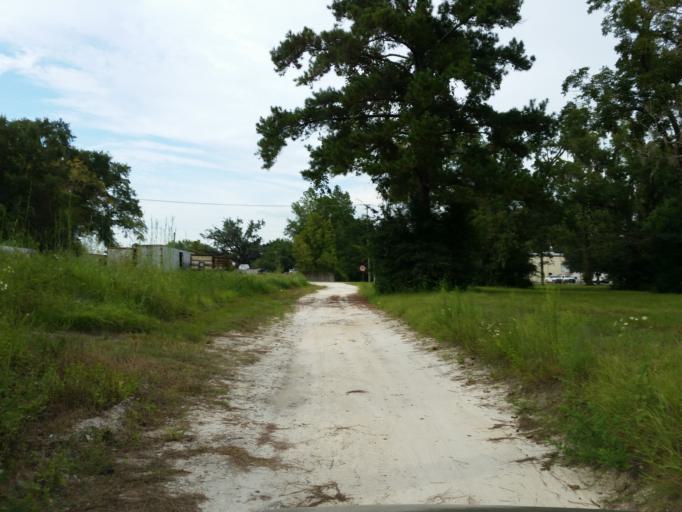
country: US
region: Florida
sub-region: Suwannee County
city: Live Oak
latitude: 30.3039
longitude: -82.9840
